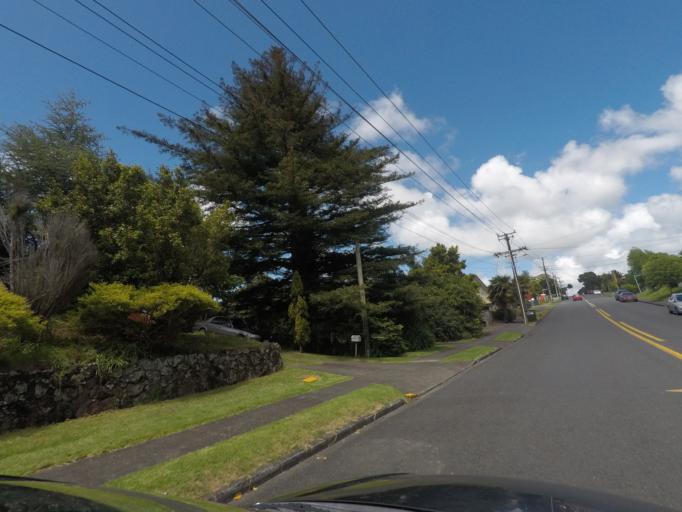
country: NZ
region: Auckland
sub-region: Auckland
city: Rosebank
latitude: -36.8768
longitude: 174.6432
